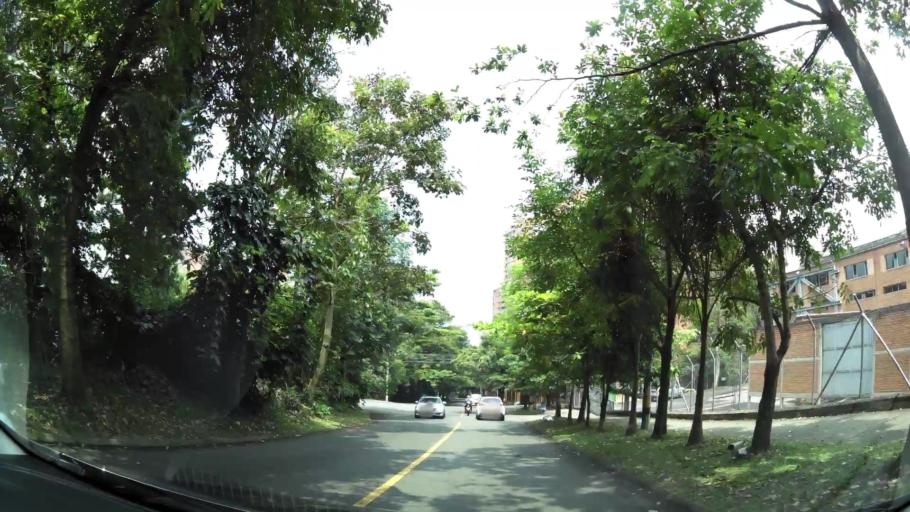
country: CO
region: Antioquia
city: Envigado
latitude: 6.2025
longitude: -75.5658
